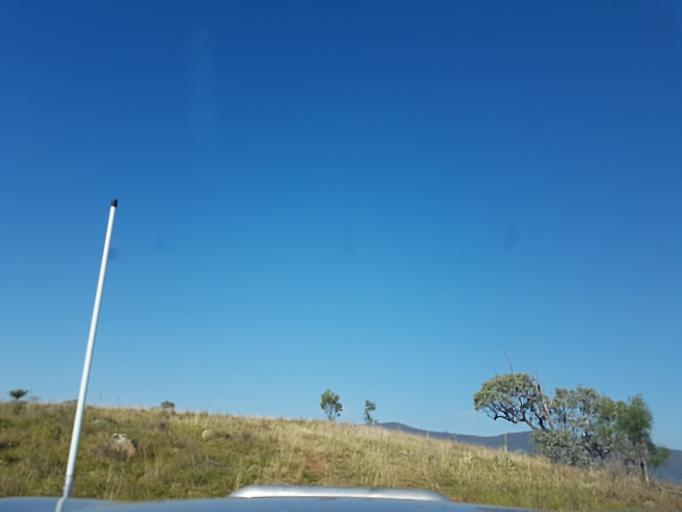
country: AU
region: New South Wales
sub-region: Snowy River
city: Jindabyne
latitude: -36.9509
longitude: 148.3467
